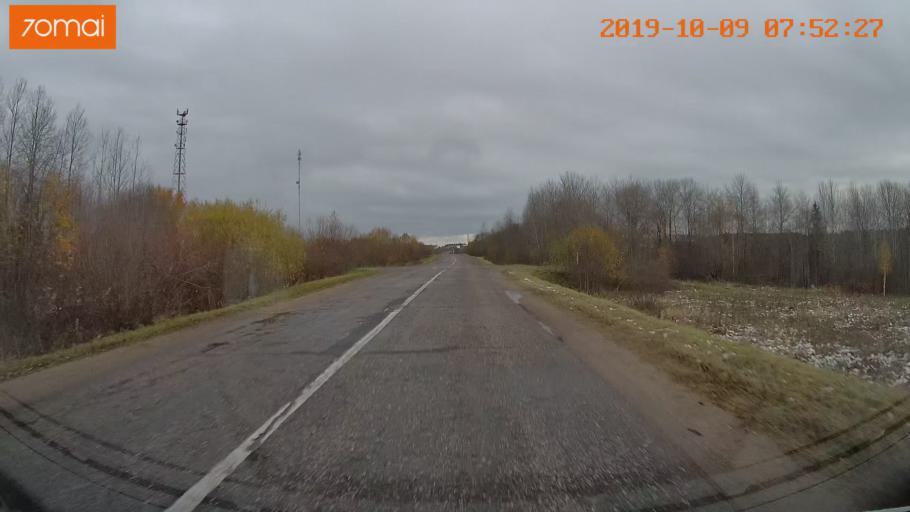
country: RU
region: Jaroslavl
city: Kukoboy
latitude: 58.6913
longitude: 39.8873
